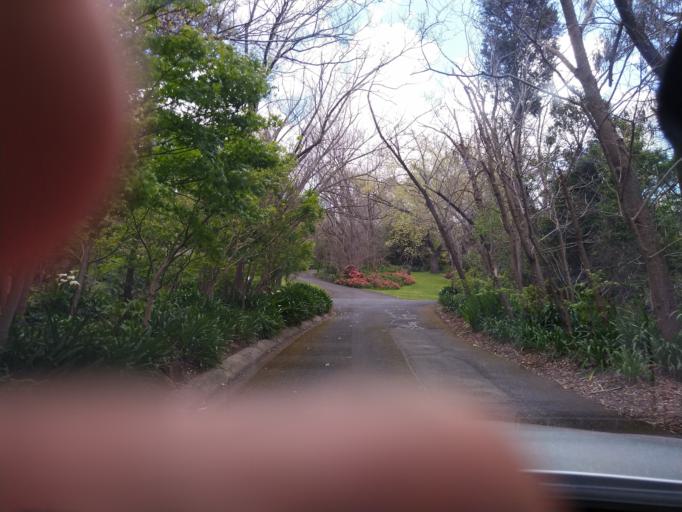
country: AU
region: Victoria
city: Rosanna
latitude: -37.7661
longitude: 145.0642
